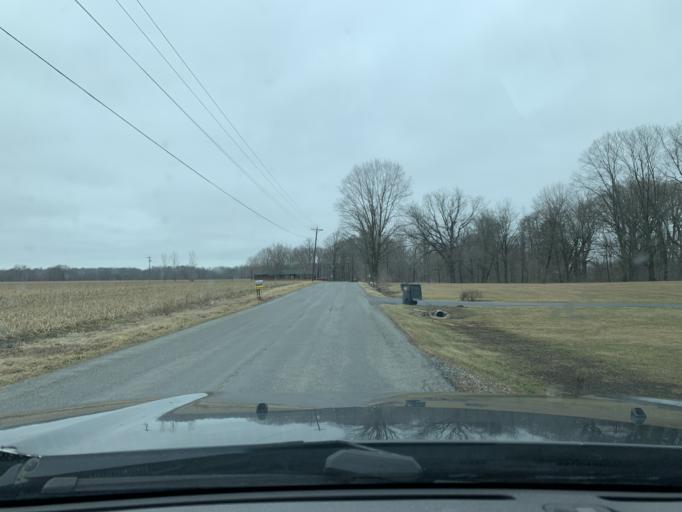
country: US
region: Indiana
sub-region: Porter County
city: Chesterton
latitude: 41.6052
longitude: -86.9901
